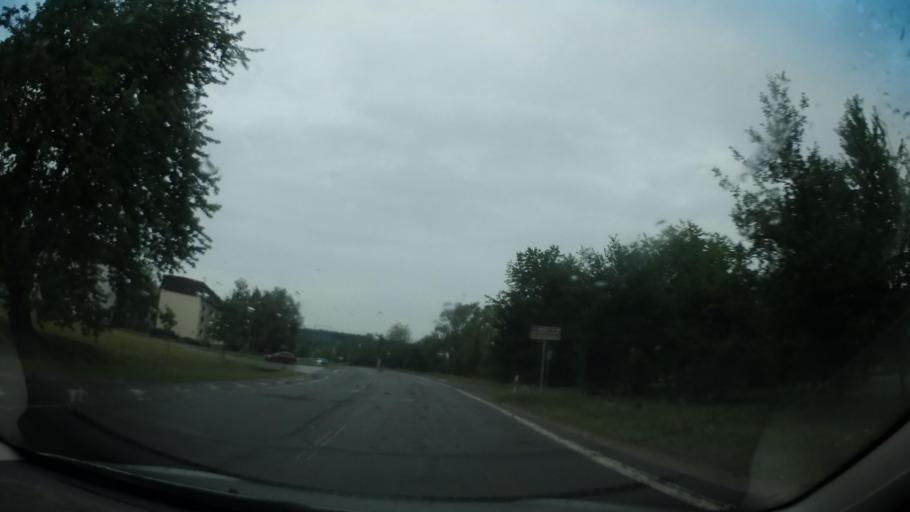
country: CZ
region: Central Bohemia
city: Milovice
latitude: 50.2319
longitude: 14.8873
